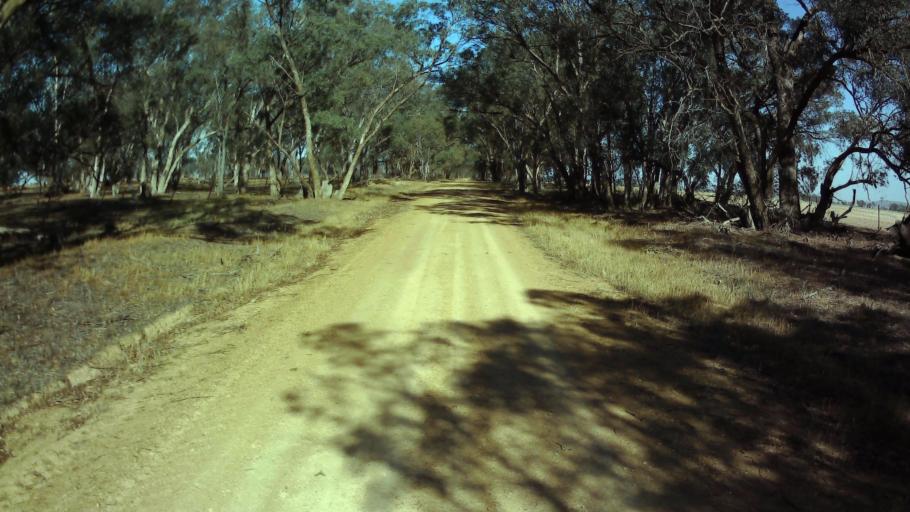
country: AU
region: New South Wales
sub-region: Weddin
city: Grenfell
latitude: -34.0495
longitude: 148.2951
